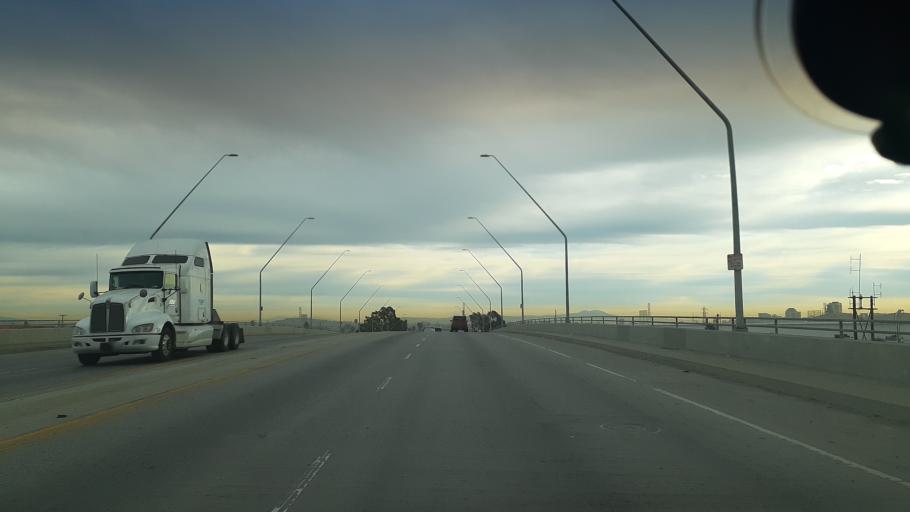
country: US
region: California
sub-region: Los Angeles County
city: Long Beach
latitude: 33.7812
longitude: -118.2381
